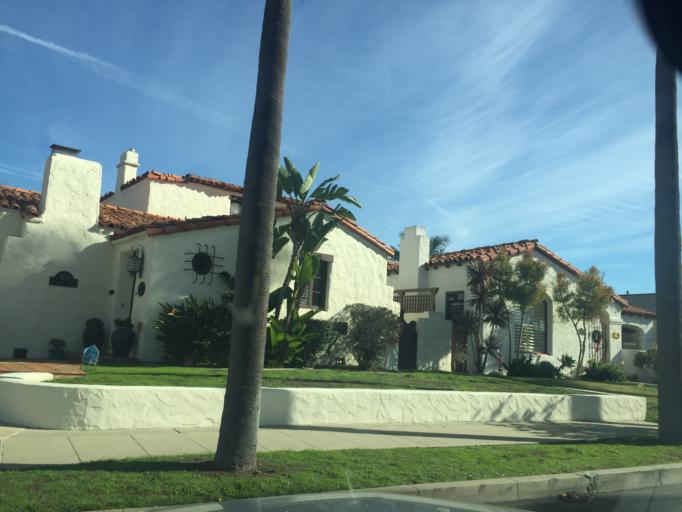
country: US
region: California
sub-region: San Diego County
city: Lemon Grove
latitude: 32.7716
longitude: -117.1032
